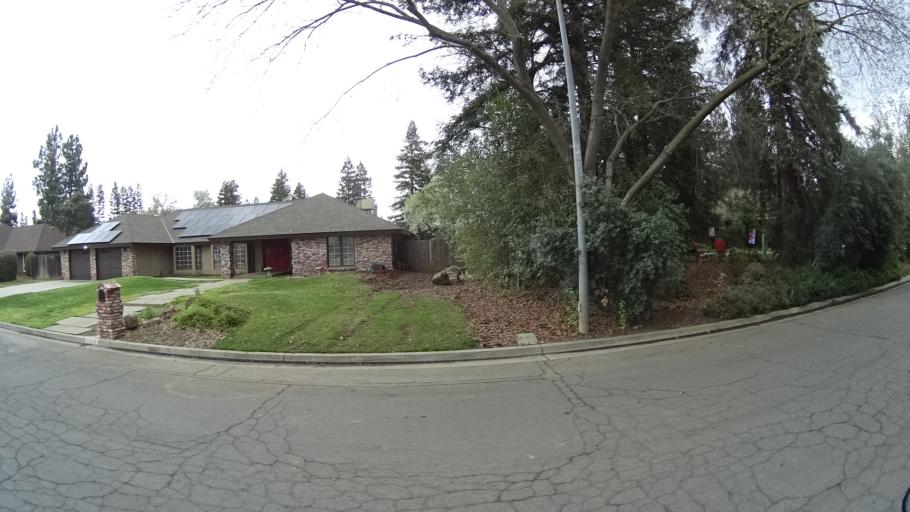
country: US
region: California
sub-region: Fresno County
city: Fresno
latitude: 36.8413
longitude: -119.8271
